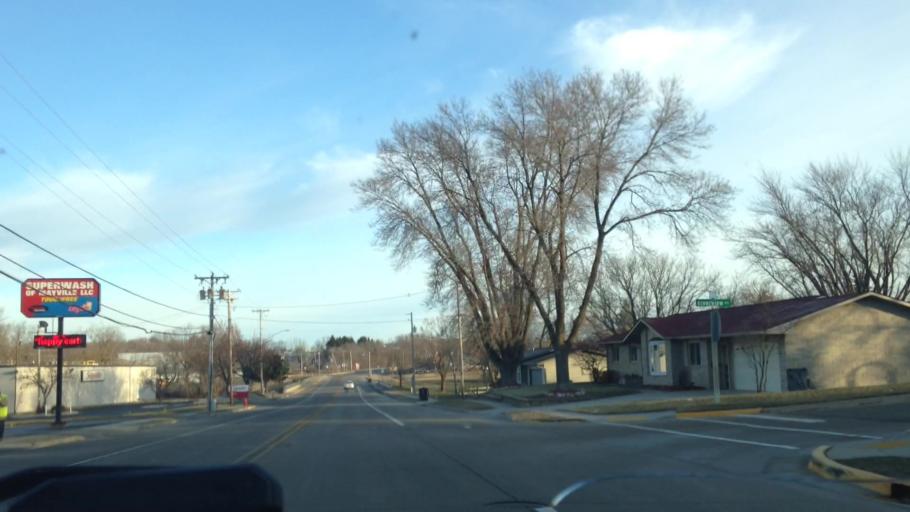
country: US
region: Wisconsin
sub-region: Dodge County
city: Mayville
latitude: 43.5055
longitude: -88.5425
